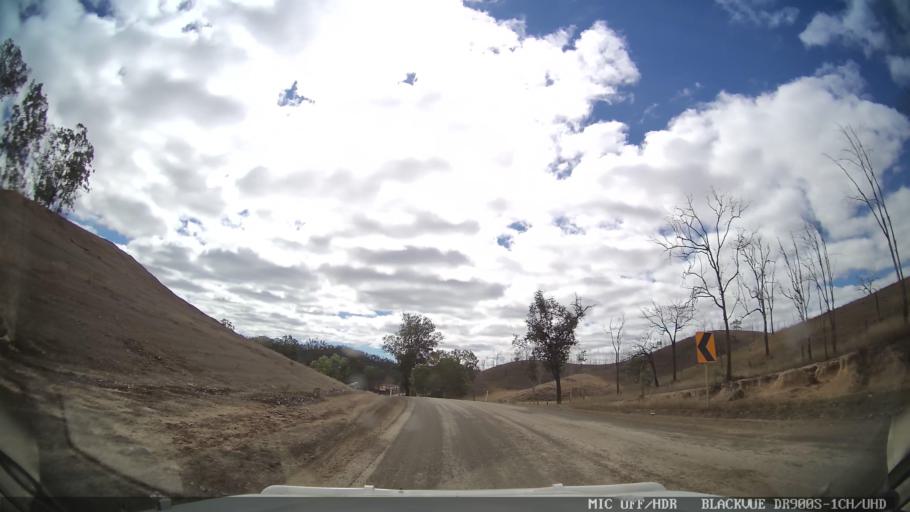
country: AU
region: Queensland
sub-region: Gladstone
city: Toolooa
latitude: -24.6179
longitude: 151.2981
